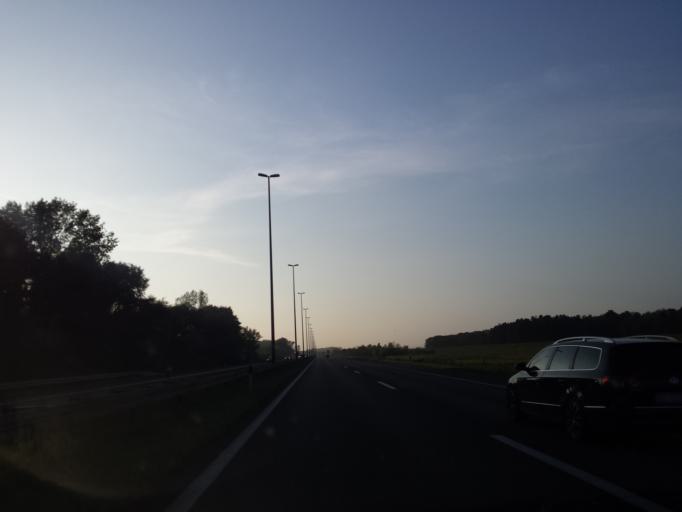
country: HR
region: Grad Zagreb
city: Lucko
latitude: 45.7779
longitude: 15.8733
